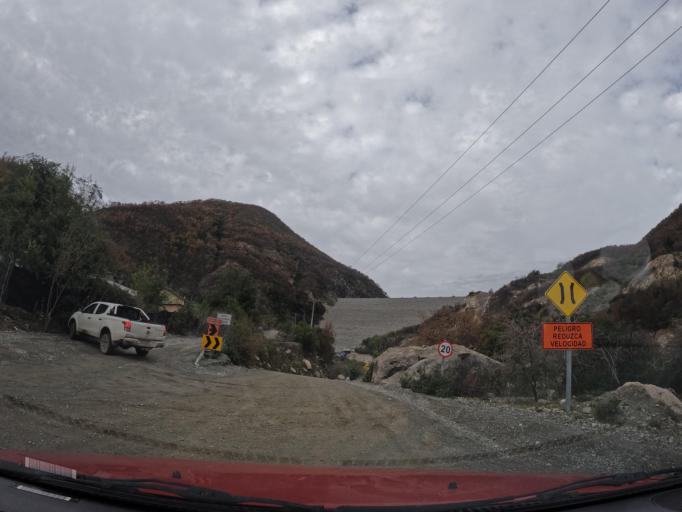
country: CL
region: Maule
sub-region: Provincia de Linares
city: Colbun
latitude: -35.8546
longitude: -71.1904
